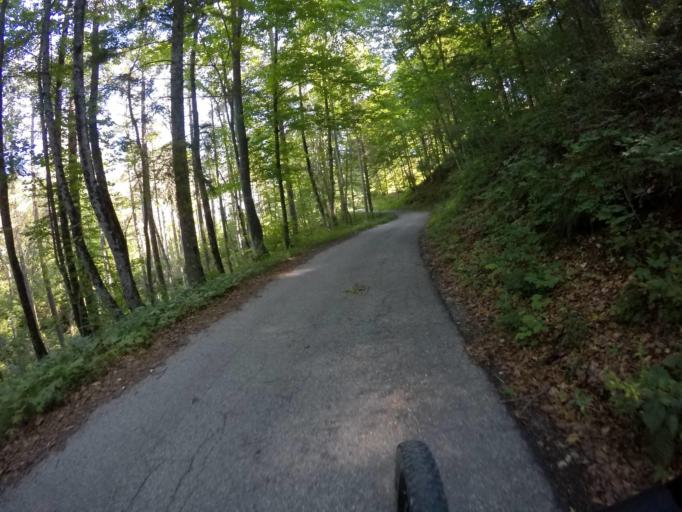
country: IT
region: Friuli Venezia Giulia
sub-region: Provincia di Udine
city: Zuglio
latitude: 46.4497
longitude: 13.0908
